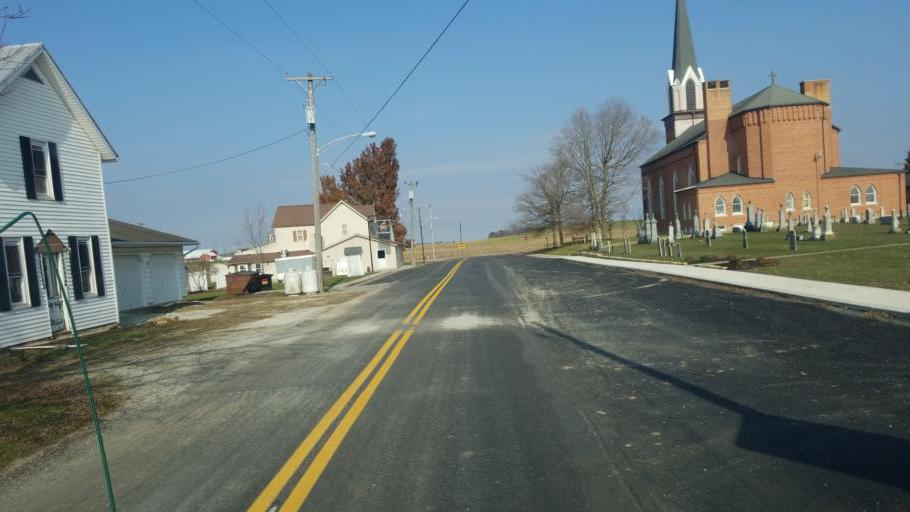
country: US
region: Ohio
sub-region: Mercer County
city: Fort Recovery
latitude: 40.4274
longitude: -84.7390
